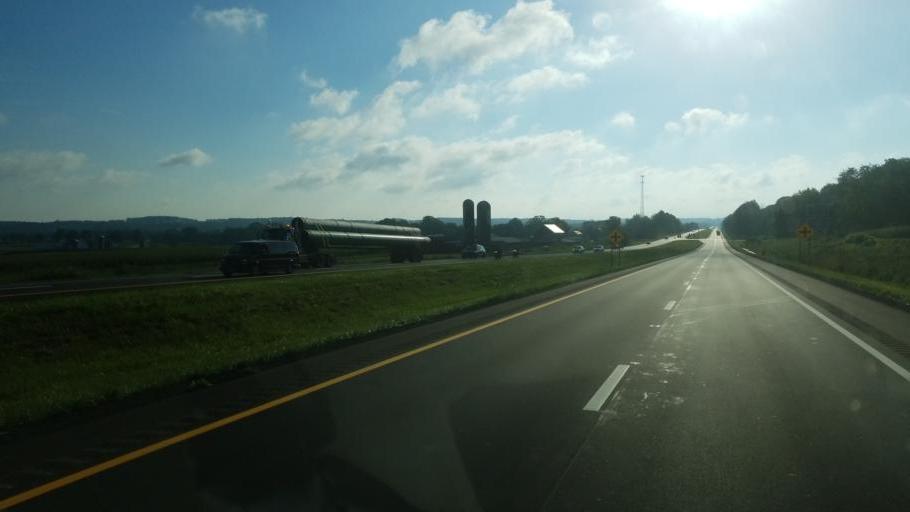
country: US
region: Ohio
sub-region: Ashland County
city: Ashland
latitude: 40.7847
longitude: -82.2249
